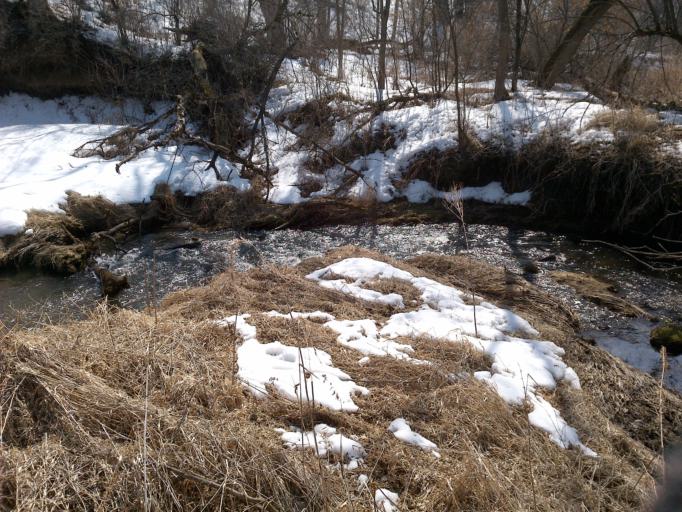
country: US
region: Minnesota
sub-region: Wabasha County
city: Lake City
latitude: 44.4373
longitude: -92.3390
